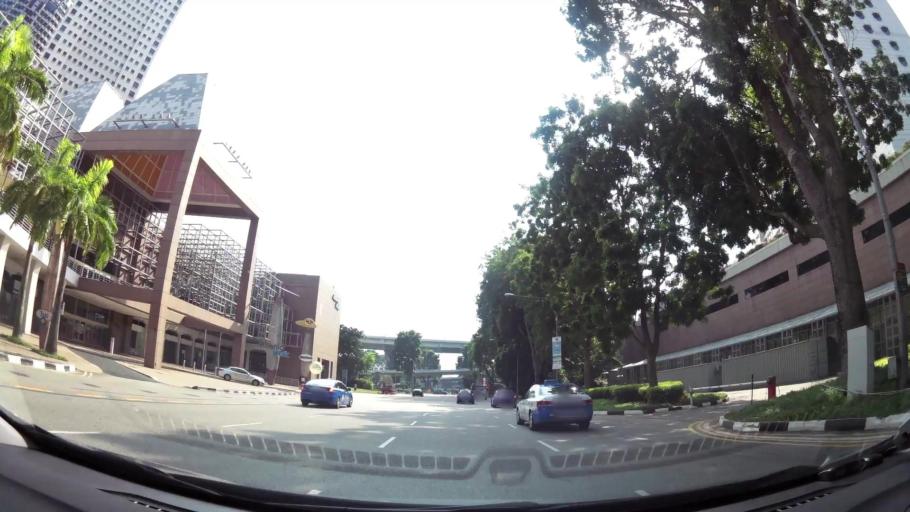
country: SG
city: Singapore
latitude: 1.2914
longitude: 103.8596
